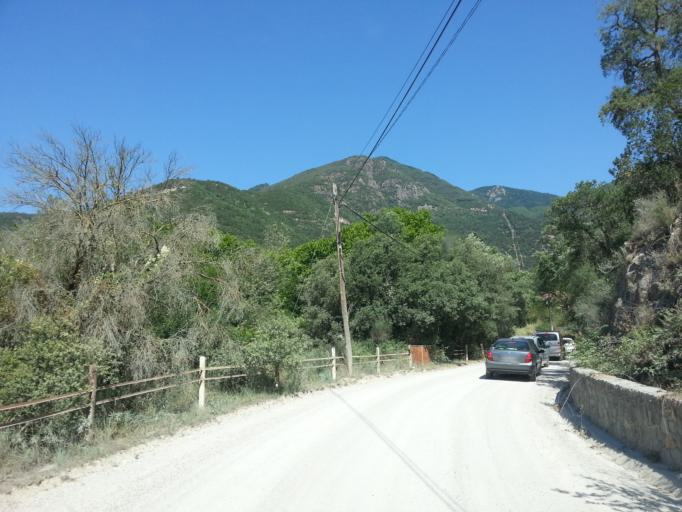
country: ES
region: Catalonia
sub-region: Provincia de Barcelona
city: Campins
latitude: 41.7391
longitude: 2.4978
